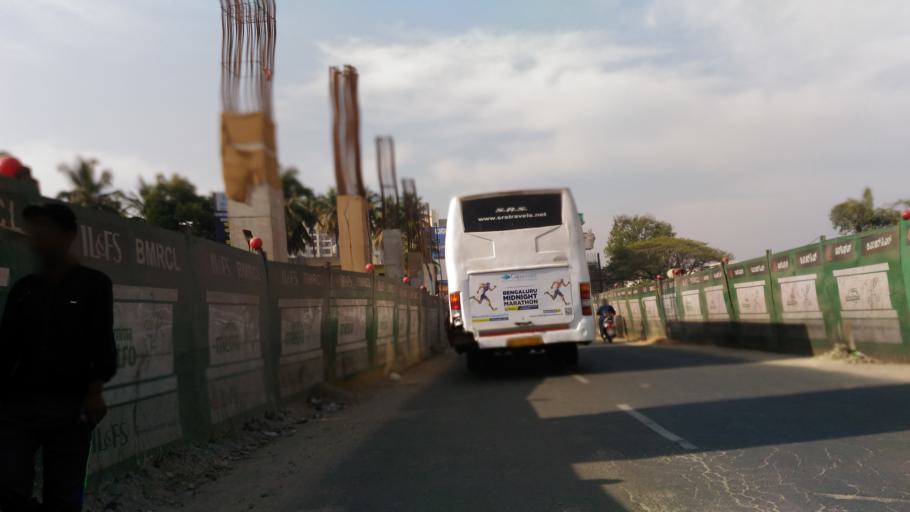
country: IN
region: Karnataka
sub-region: Bangalore Urban
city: Bangalore
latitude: 12.9419
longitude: 77.5253
